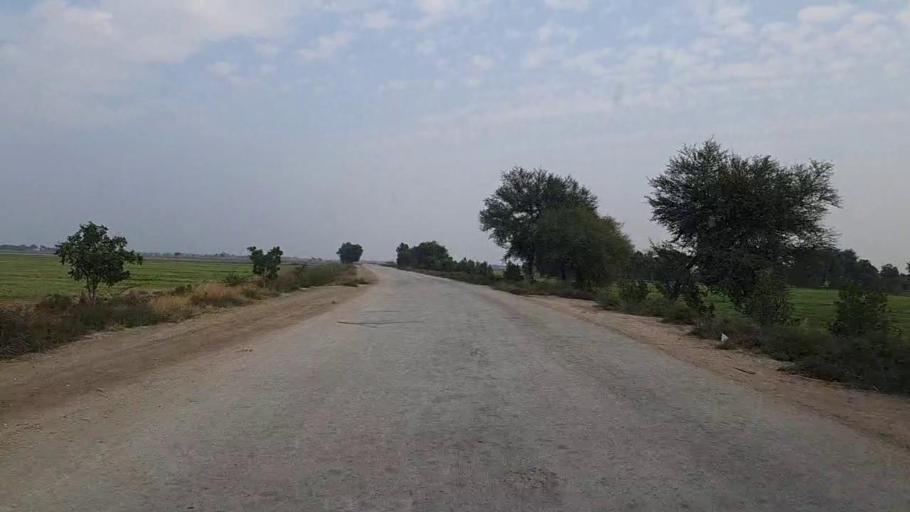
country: PK
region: Sindh
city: Mirwah Gorchani
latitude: 25.3936
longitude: 69.0741
